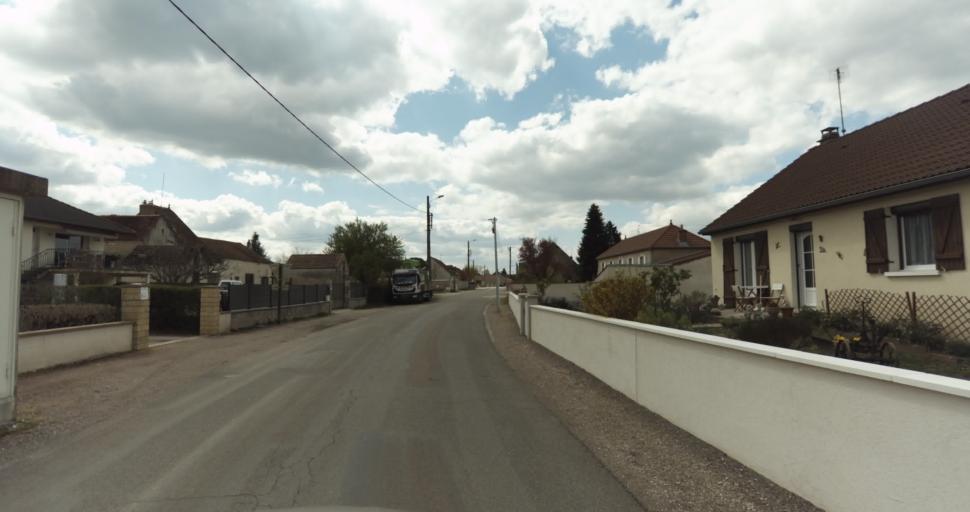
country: FR
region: Bourgogne
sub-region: Departement de la Cote-d'Or
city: Auxonne
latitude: 47.1860
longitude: 5.3984
